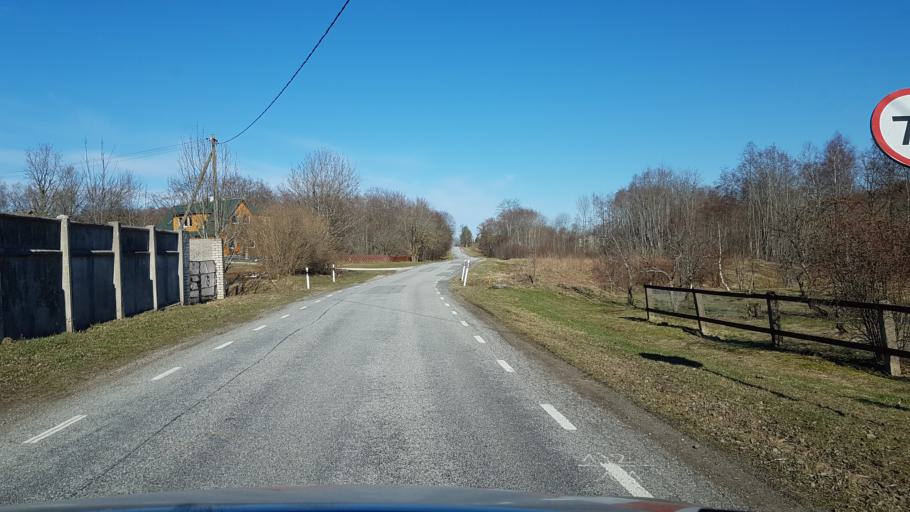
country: EE
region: Laeaene-Virumaa
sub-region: Kadrina vald
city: Kadrina
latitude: 59.3509
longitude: 26.1111
